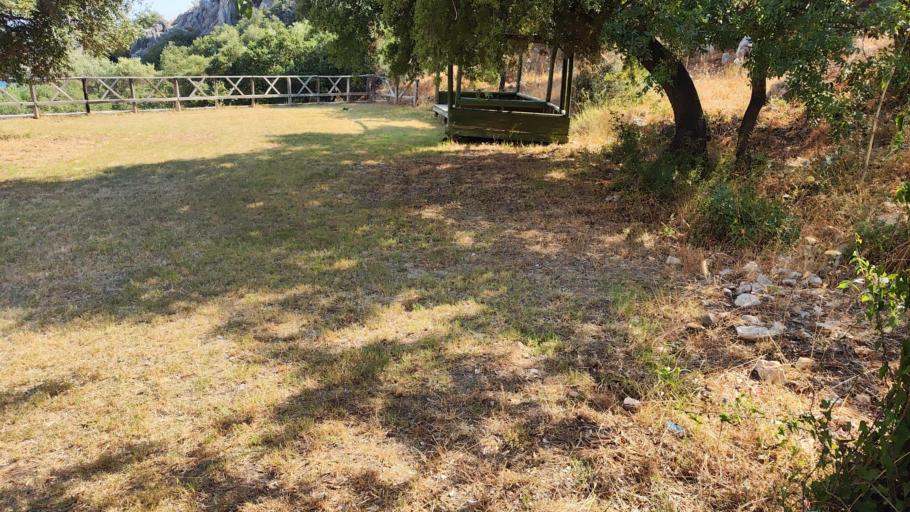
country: TR
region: Mugla
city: Sarigerme
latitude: 36.7048
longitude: 28.6936
